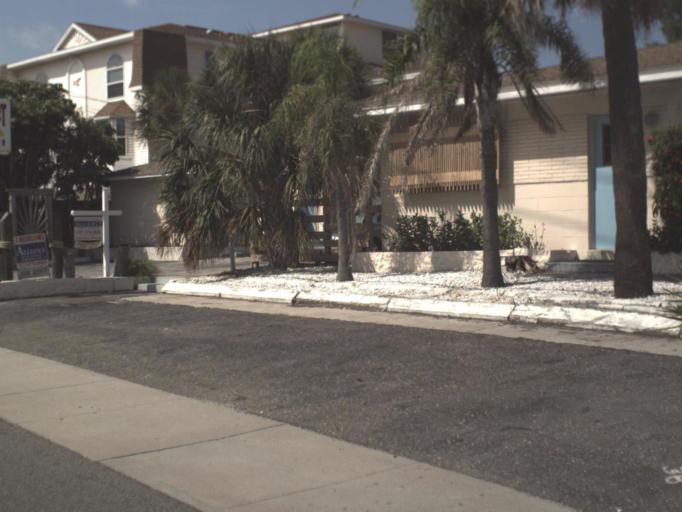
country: US
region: Florida
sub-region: Pinellas County
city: Treasure Island
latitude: 27.7621
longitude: -82.7665
